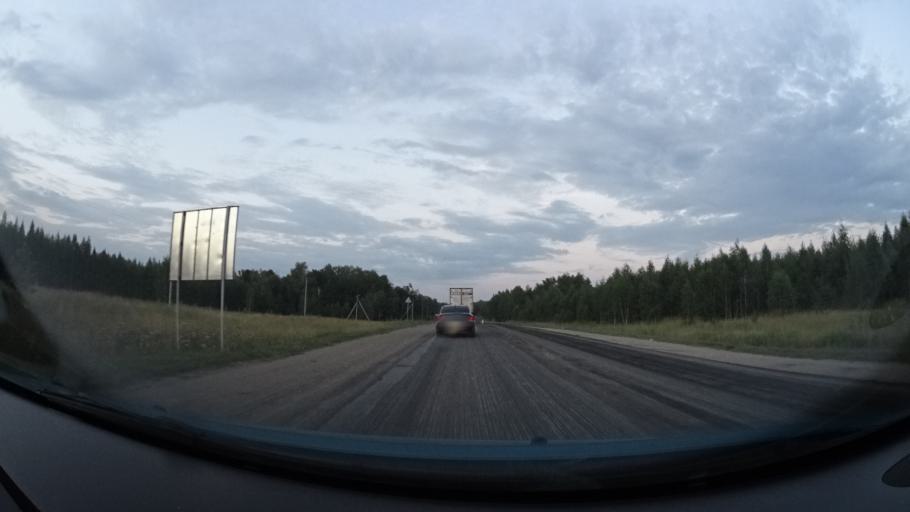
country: RU
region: Tatarstan
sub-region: Bugul'minskiy Rayon
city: Bugul'ma
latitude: 54.2640
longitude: 52.9344
